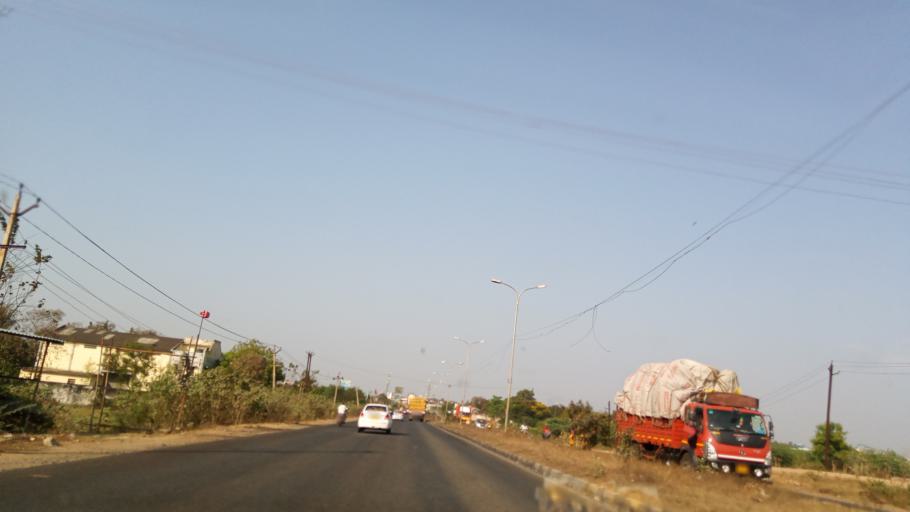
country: IN
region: Tamil Nadu
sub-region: Kancheepuram
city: Sriperumbudur
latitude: 12.9899
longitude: 79.9824
